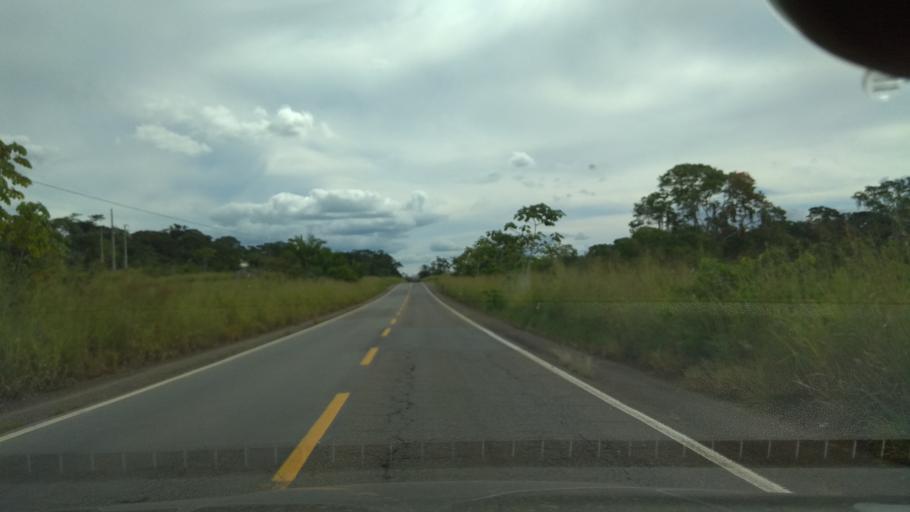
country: BR
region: Bahia
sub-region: Ipiau
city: Ipiau
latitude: -14.1947
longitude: -39.6410
